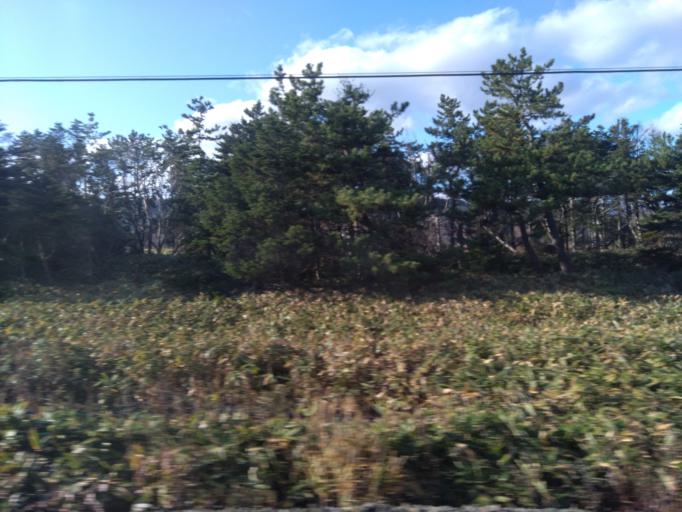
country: JP
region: Hokkaido
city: Niseko Town
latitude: 42.5788
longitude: 140.4531
